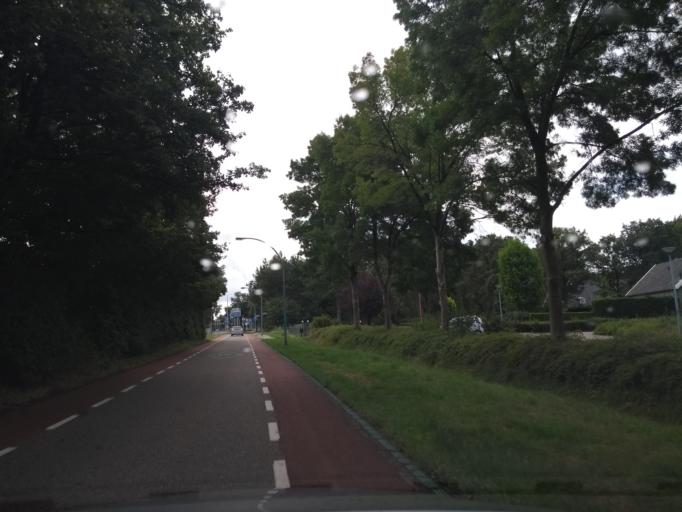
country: NL
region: Overijssel
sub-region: Gemeente Almelo
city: Almelo
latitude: 52.3602
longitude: 6.6728
